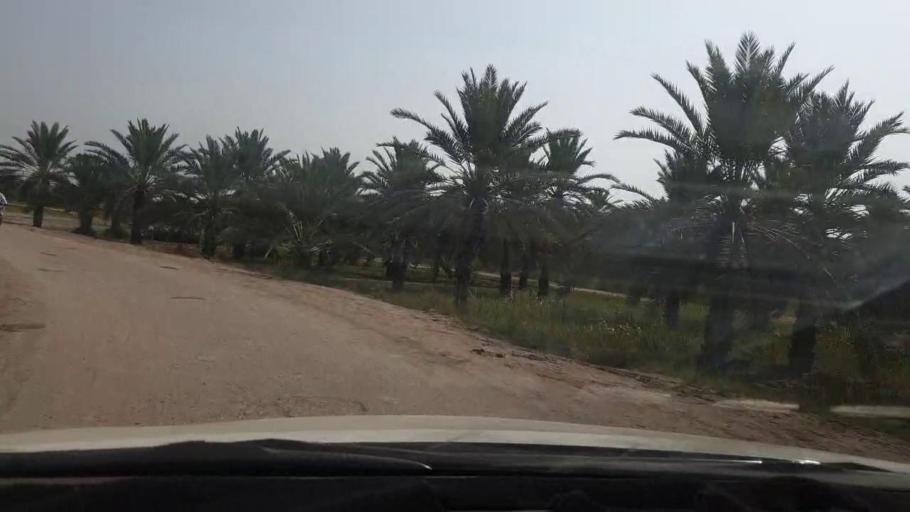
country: PK
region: Sindh
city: Rohri
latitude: 27.5886
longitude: 68.8738
